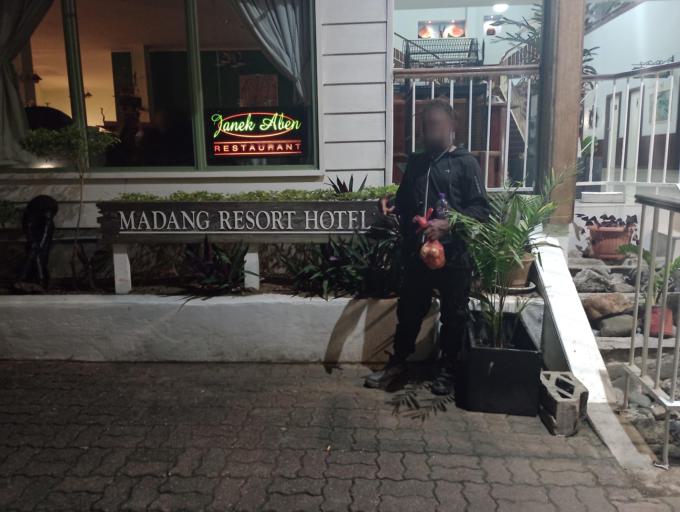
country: PG
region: Madang
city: Madang
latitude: -5.2083
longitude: 145.8104
